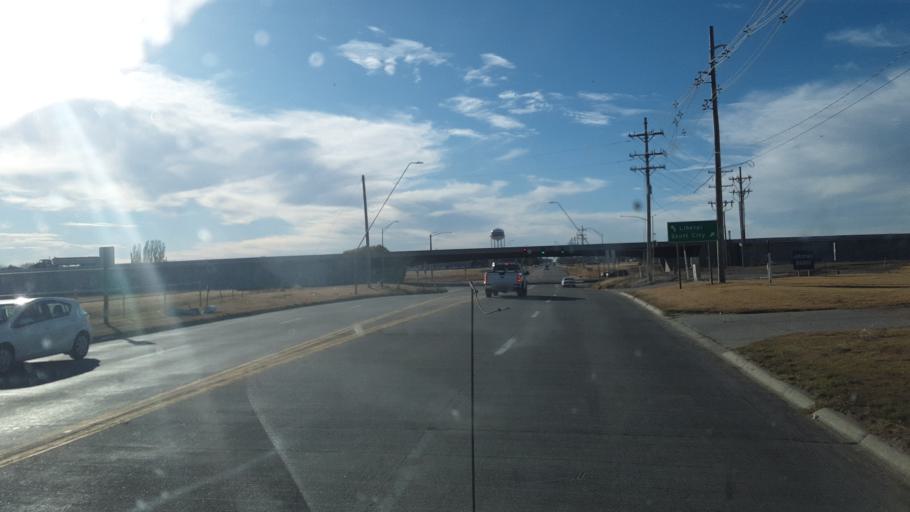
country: US
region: Kansas
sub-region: Finney County
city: Garden City
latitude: 37.9894
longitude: -100.8367
